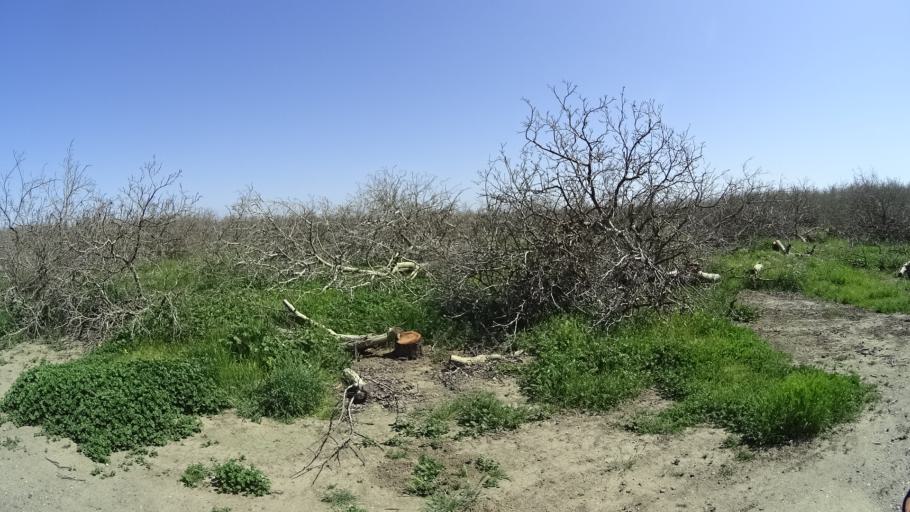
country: US
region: California
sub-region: Glenn County
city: Willows
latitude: 39.4407
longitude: -121.9863
